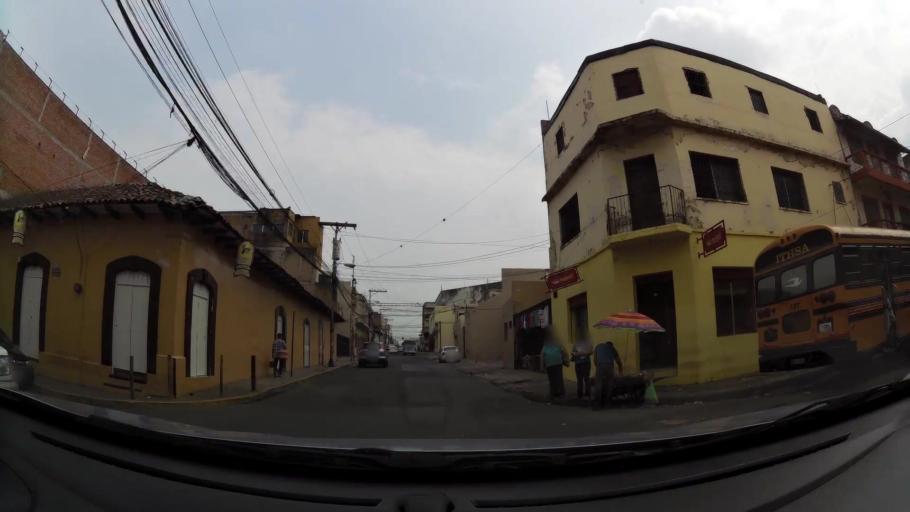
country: HN
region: Francisco Morazan
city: Tegucigalpa
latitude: 14.0980
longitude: -87.2081
